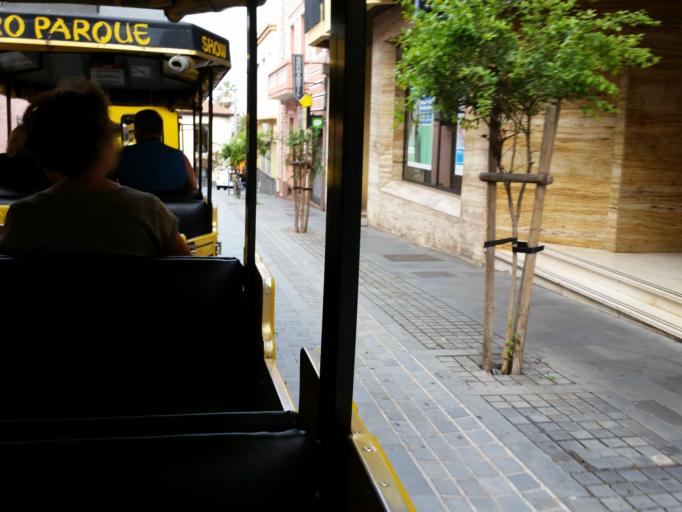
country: ES
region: Canary Islands
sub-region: Provincia de Santa Cruz de Tenerife
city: Puerto de la Cruz
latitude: 28.4163
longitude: -16.5476
